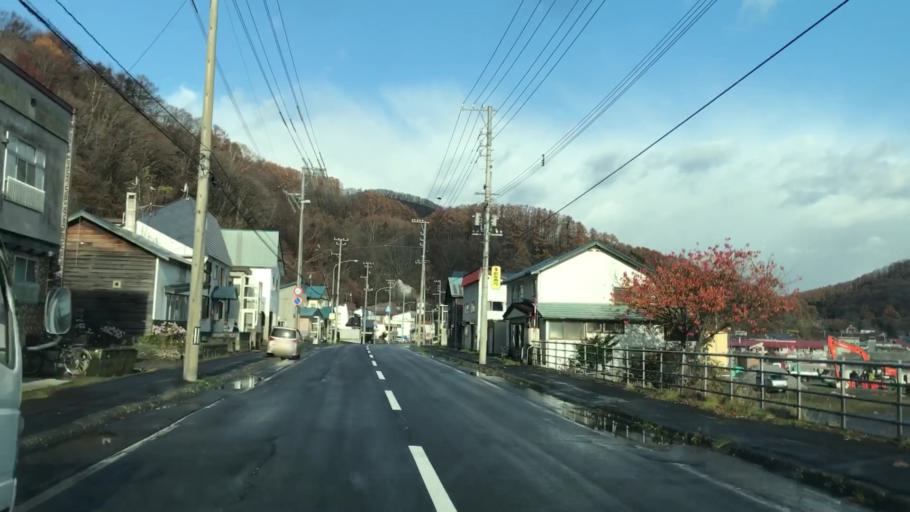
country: JP
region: Hokkaido
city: Yoichi
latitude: 43.2714
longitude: 140.6367
